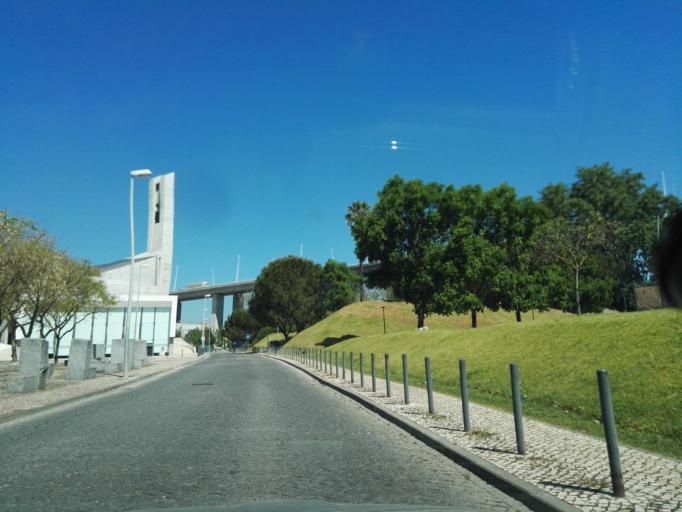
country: PT
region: Lisbon
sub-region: Loures
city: Moscavide
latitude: 38.7845
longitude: -9.0948
